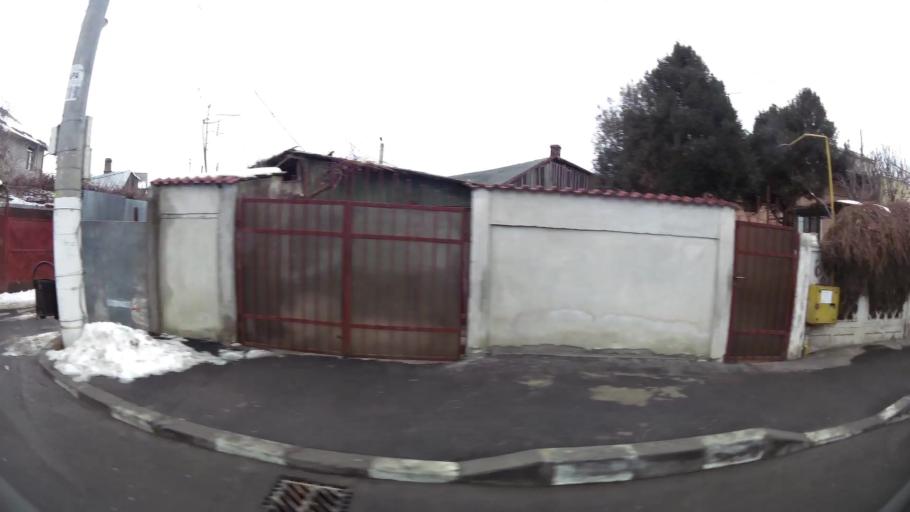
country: RO
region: Ilfov
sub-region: Comuna Pantelimon
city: Pantelimon
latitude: 44.4465
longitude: 26.1984
